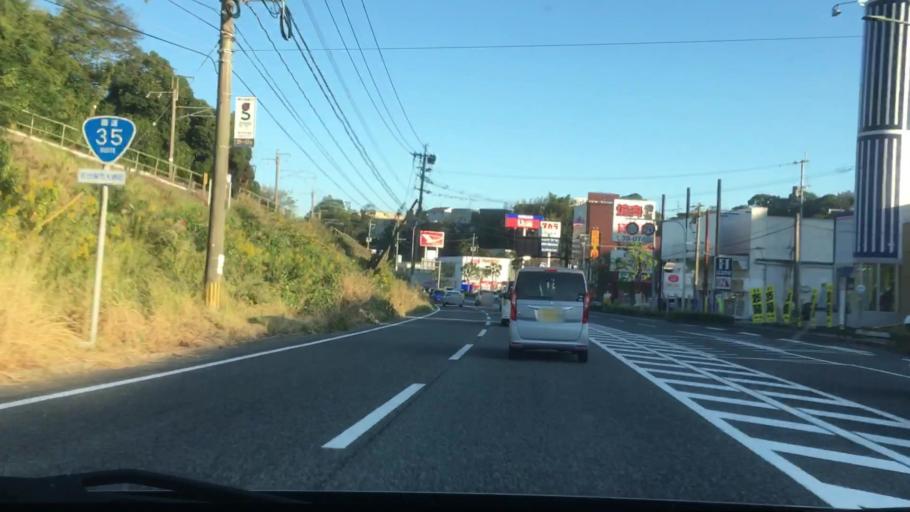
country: JP
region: Nagasaki
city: Sasebo
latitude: 33.1542
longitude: 129.7731
